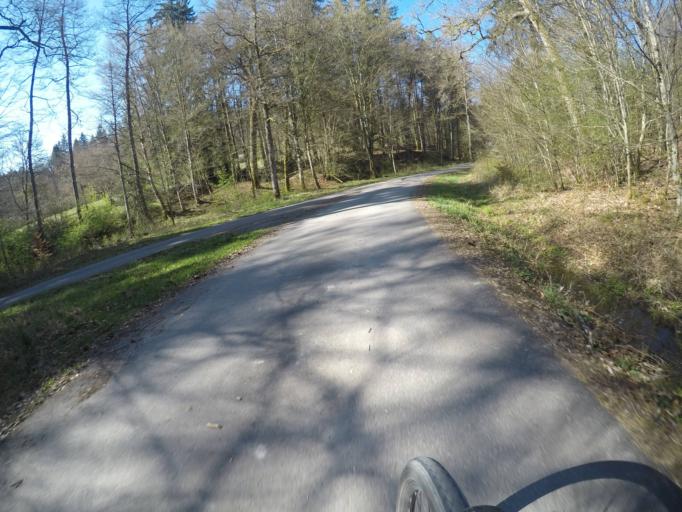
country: DE
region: Baden-Wuerttemberg
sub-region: Tuebingen Region
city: Tuebingen
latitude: 48.5575
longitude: 9.0147
